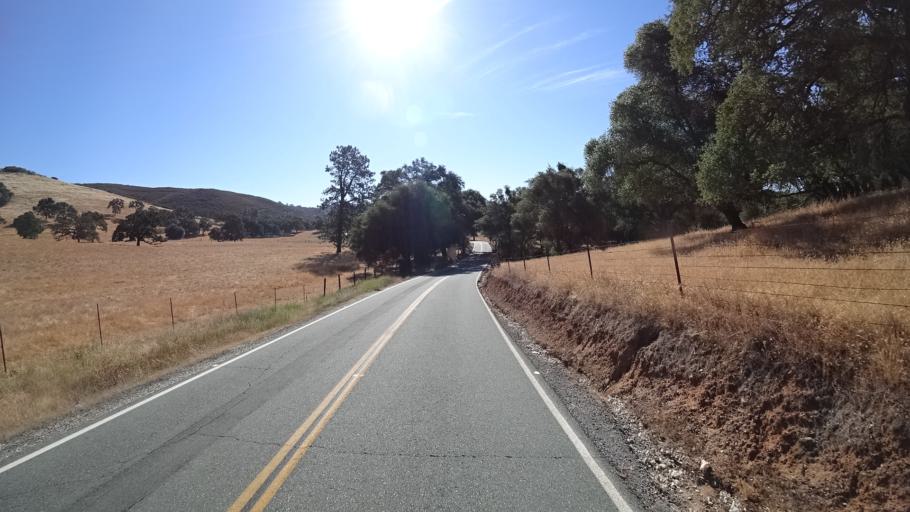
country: US
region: California
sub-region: Calaveras County
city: San Andreas
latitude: 38.1710
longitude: -120.6373
